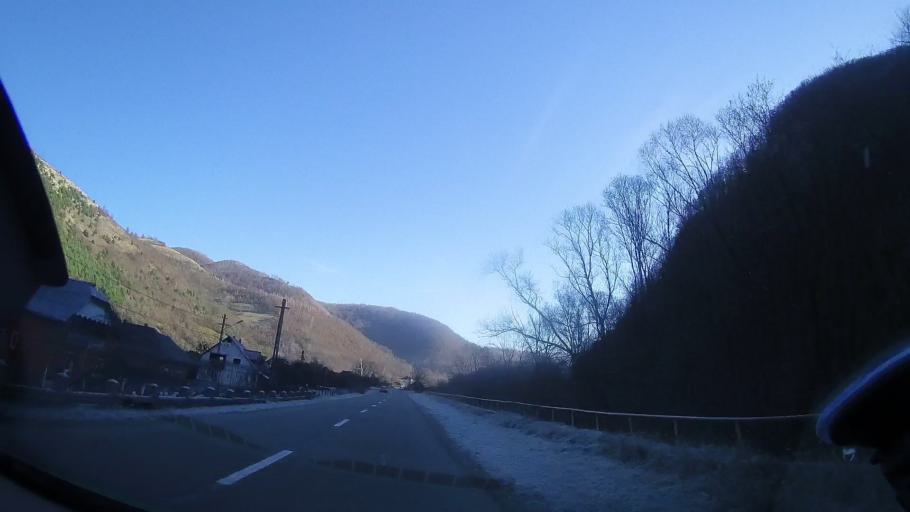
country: RO
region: Bihor
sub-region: Comuna Bulz
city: Bulz
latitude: 46.9143
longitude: 22.6687
